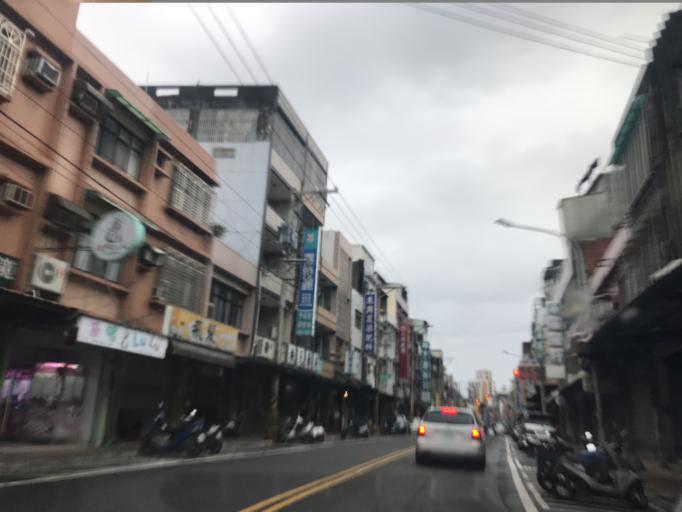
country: TW
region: Taiwan
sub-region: Hsinchu
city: Zhubei
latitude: 24.8278
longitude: 121.0783
